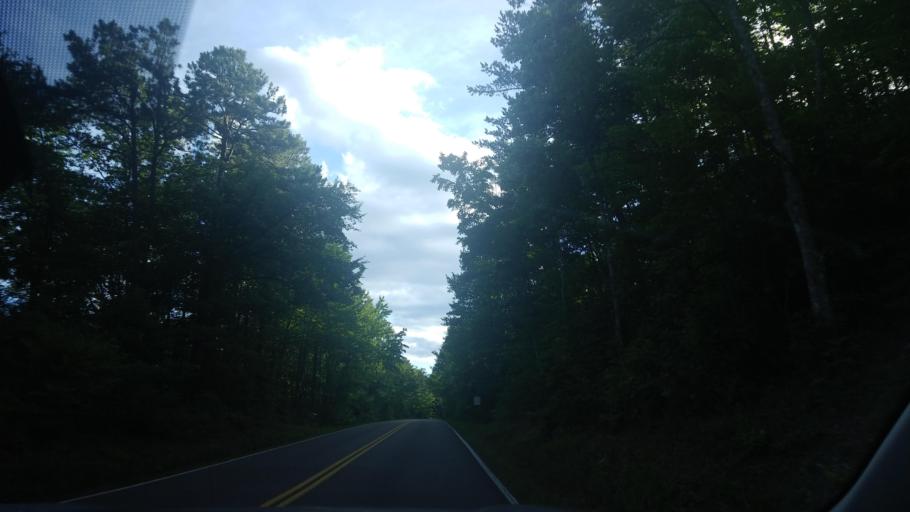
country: US
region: Tennessee
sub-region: Cocke County
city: Newport
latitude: 35.8163
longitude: -83.2189
